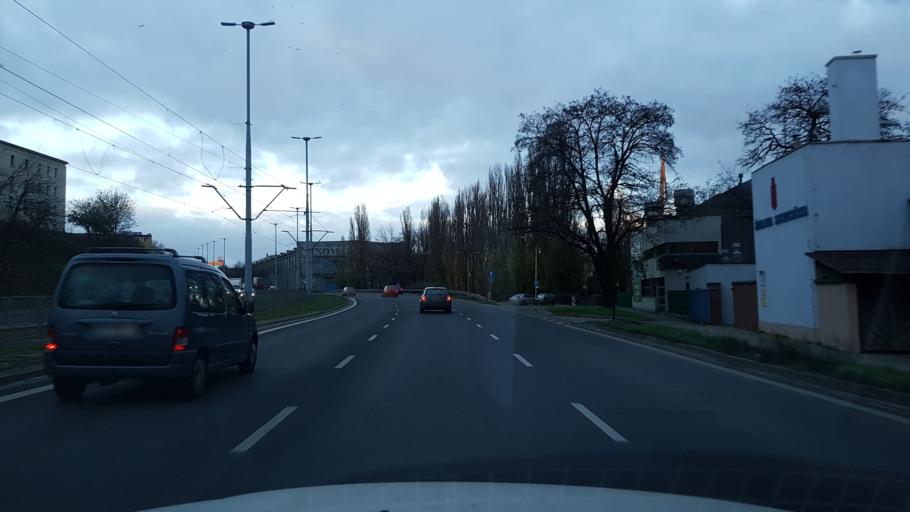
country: PL
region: West Pomeranian Voivodeship
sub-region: Szczecin
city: Szczecin
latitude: 53.4330
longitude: 14.5718
